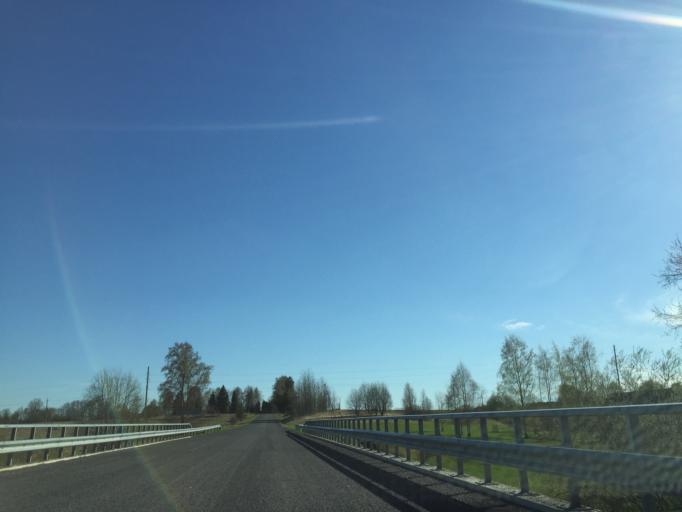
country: EE
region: Valgamaa
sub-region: Valga linn
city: Valga
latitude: 57.8381
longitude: 26.2353
